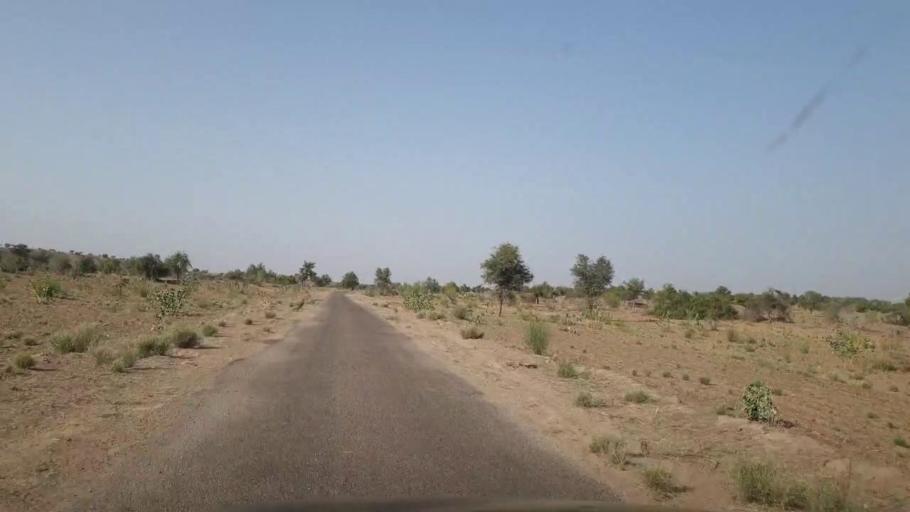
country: PK
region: Sindh
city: Islamkot
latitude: 25.1385
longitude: 70.5183
